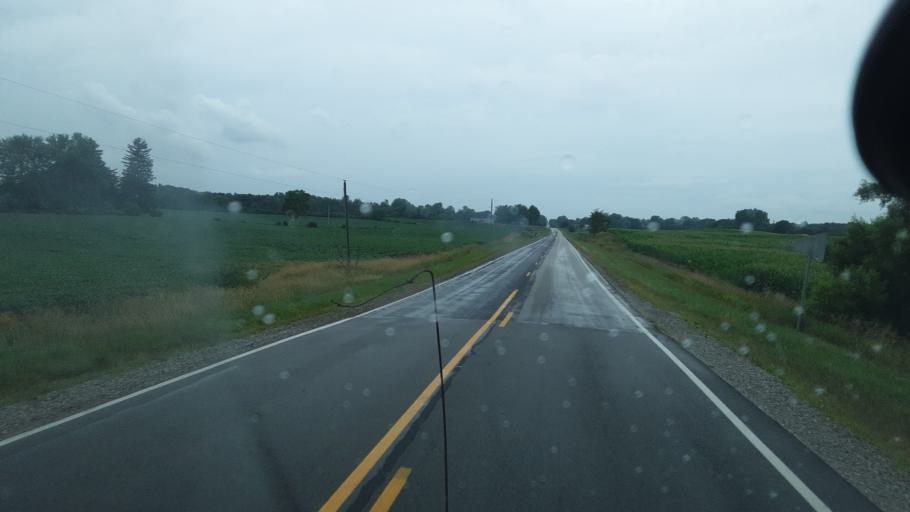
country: US
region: Indiana
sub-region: Steuben County
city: Hamilton
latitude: 41.5591
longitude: -84.8193
